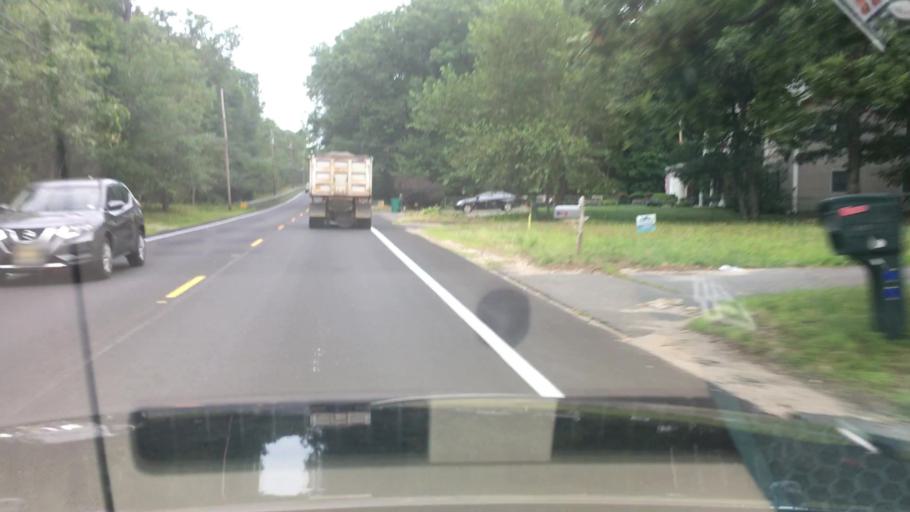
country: US
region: New Jersey
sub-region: Ocean County
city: Lakehurst
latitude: 40.0538
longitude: -74.3441
